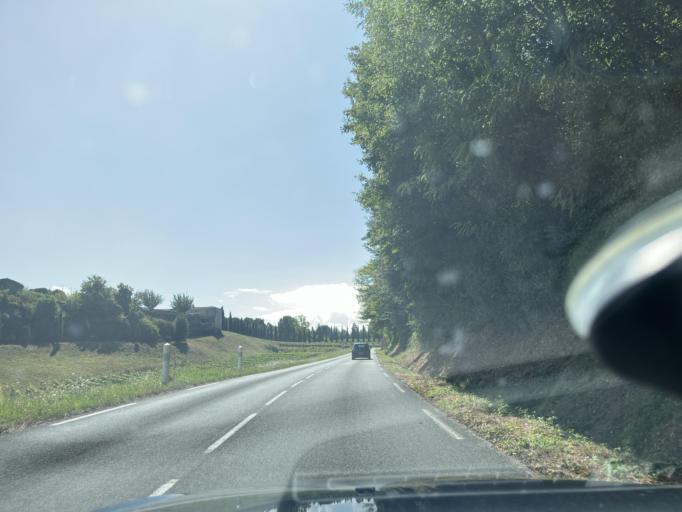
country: FR
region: Aquitaine
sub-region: Departement de la Gironde
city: Berson
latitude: 45.0774
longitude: -0.6311
